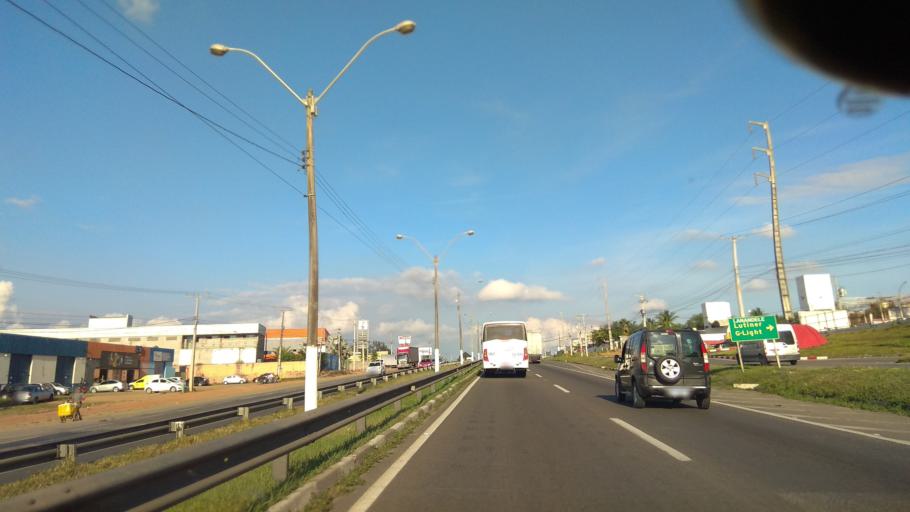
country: BR
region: Bahia
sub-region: Feira De Santana
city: Feira de Santana
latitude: -12.2914
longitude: -38.9102
